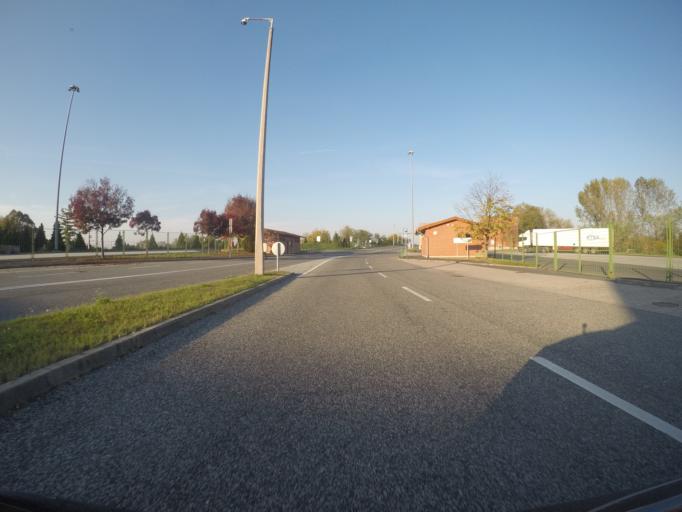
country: HU
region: Somogy
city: Barcs
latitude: 45.9482
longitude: 17.4628
